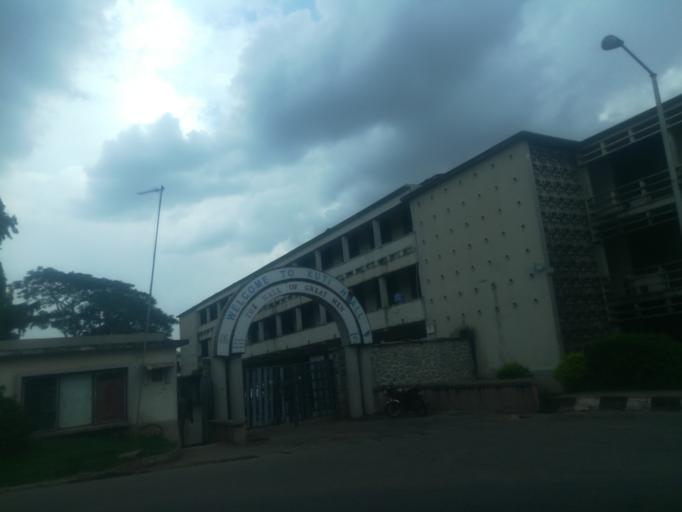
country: NG
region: Oyo
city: Ibadan
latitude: 7.4433
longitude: 3.8995
